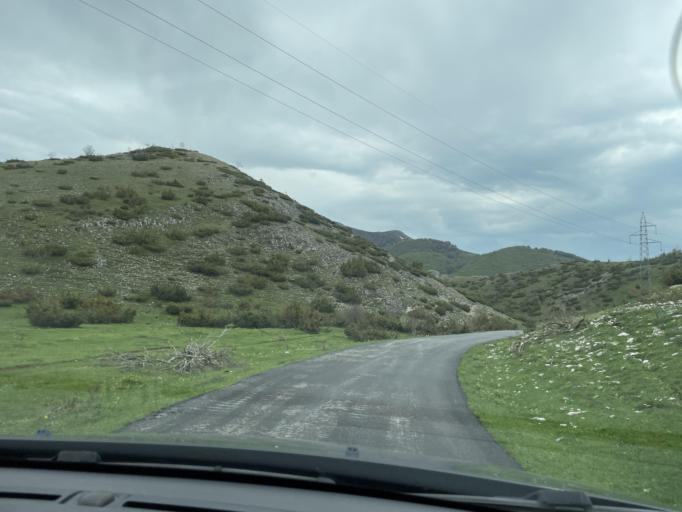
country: MK
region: Opstina Rostusa
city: Rostusha
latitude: 41.6101
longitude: 20.6804
